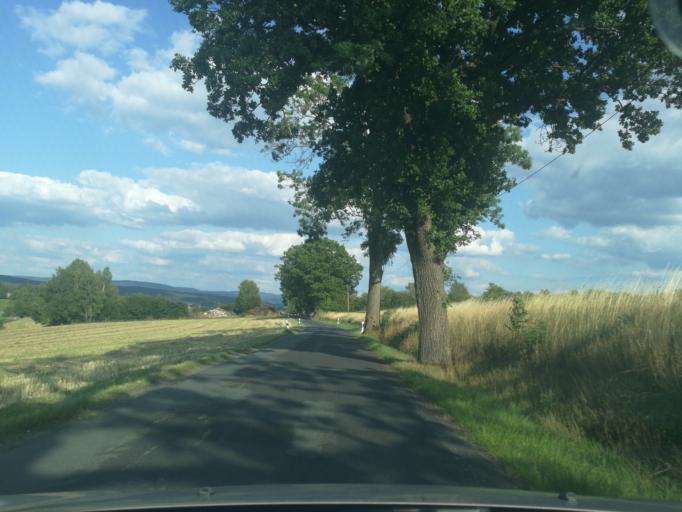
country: DE
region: Saxony
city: Adorf
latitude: 50.3163
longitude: 12.2341
